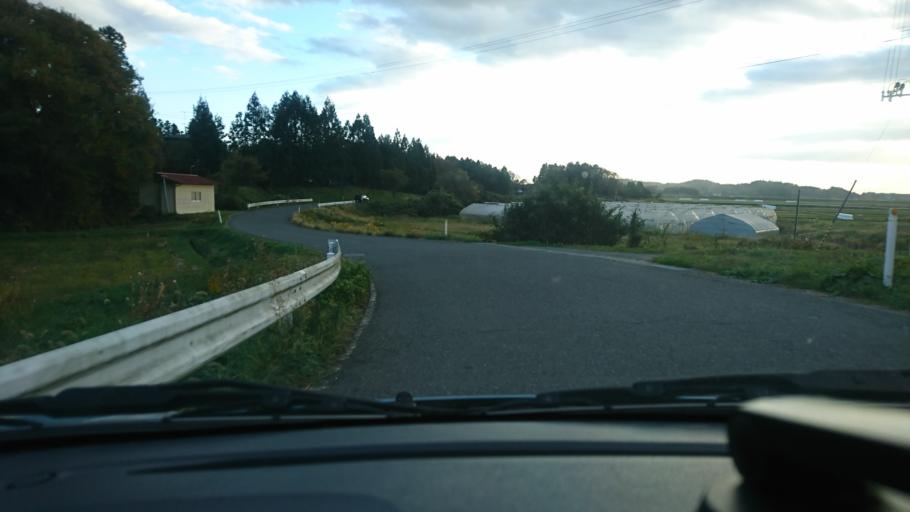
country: JP
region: Iwate
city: Ichinoseki
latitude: 38.7793
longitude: 141.2160
